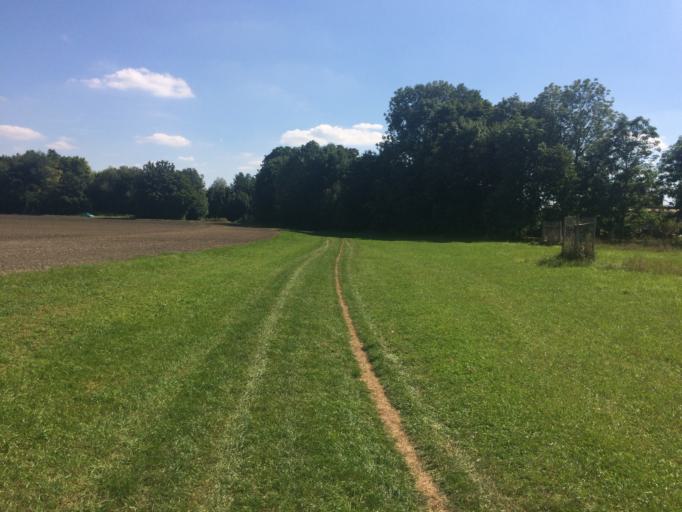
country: DE
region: Bavaria
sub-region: Swabia
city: Augsburg
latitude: 48.4042
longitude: 10.9167
